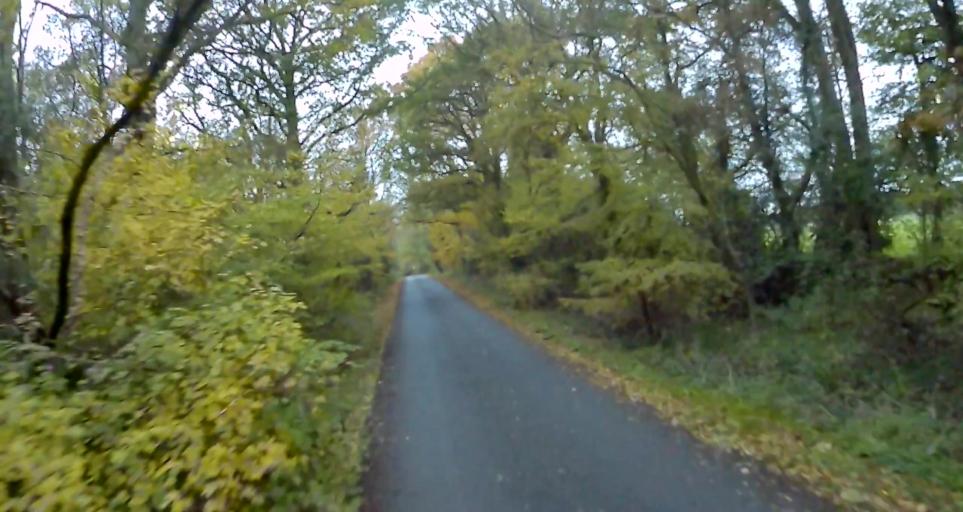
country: GB
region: England
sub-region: Hampshire
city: Odiham
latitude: 51.2471
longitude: -0.9064
